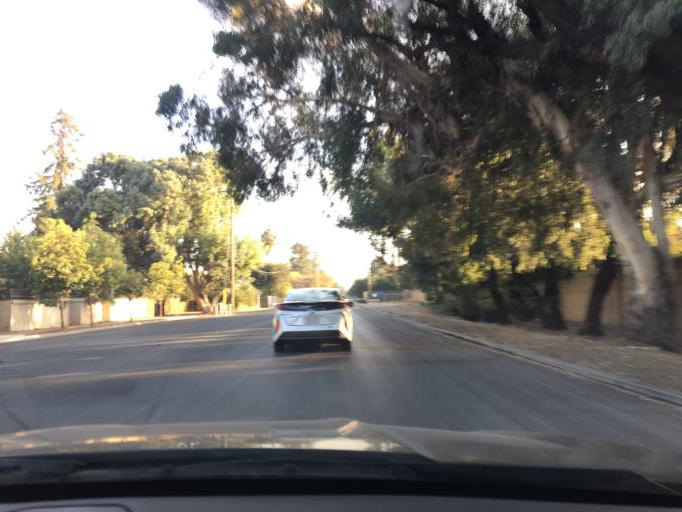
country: US
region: California
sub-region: Santa Clara County
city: Mountain View
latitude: 37.3639
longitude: -122.0779
